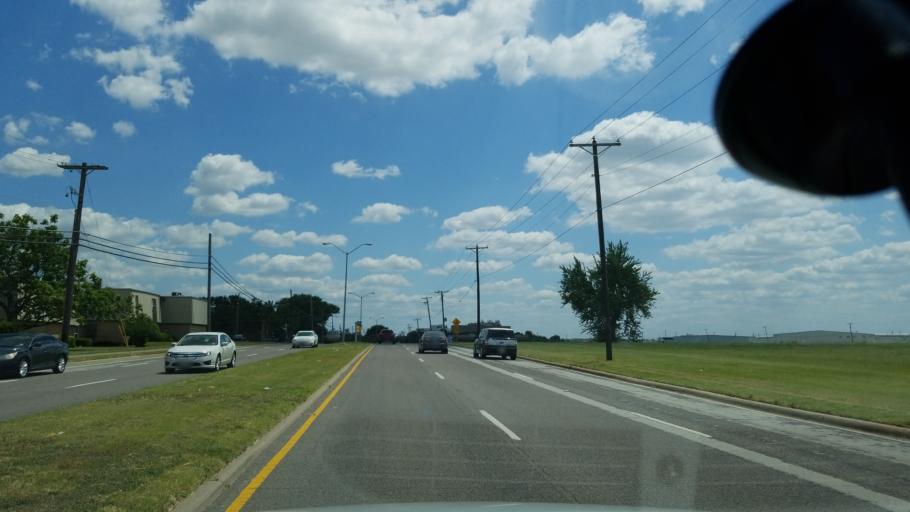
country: US
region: Texas
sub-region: Dallas County
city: Cockrell Hill
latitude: 32.6842
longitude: -96.8572
